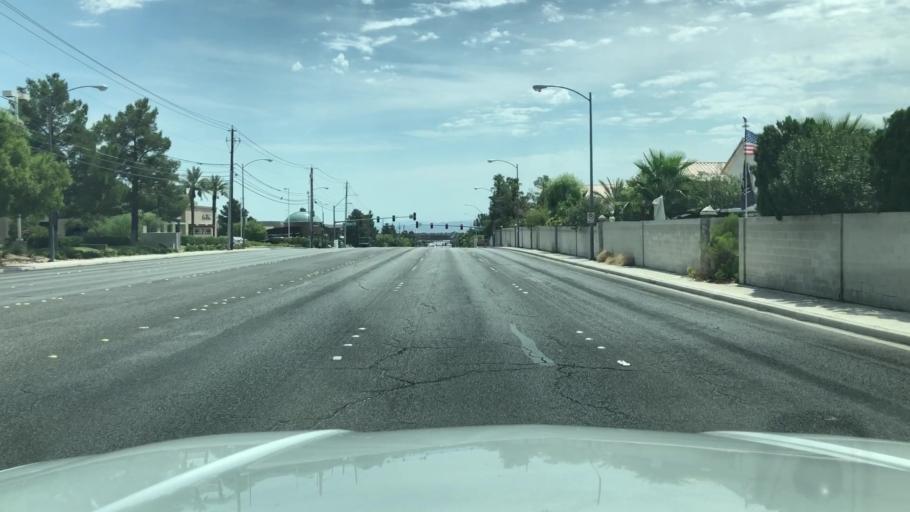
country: US
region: Nevada
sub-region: Clark County
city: Paradise
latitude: 36.0569
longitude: -115.1521
